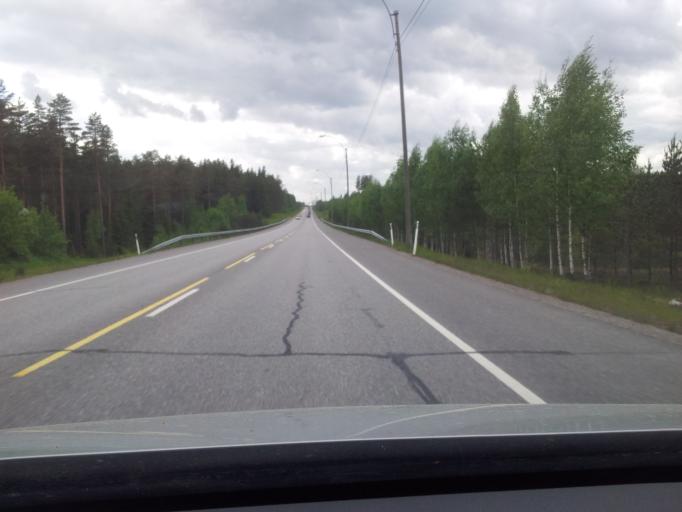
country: FI
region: South Karelia
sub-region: Lappeenranta
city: Taavetti
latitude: 60.9256
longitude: 27.5627
